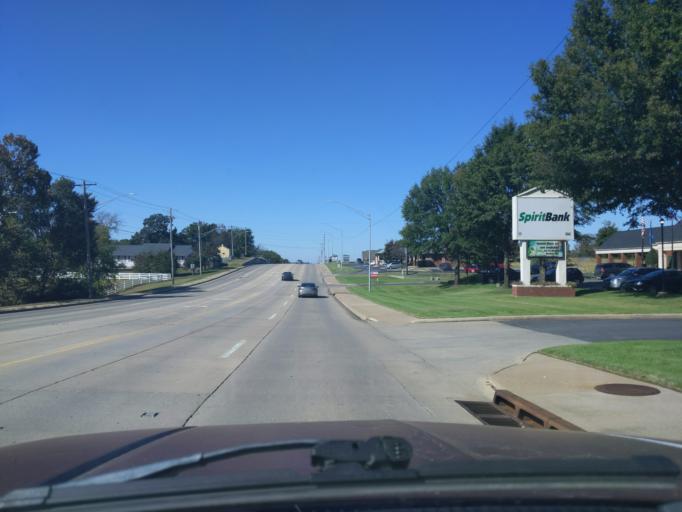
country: US
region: Oklahoma
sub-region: Creek County
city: Sapulpa
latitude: 35.9885
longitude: -96.0922
